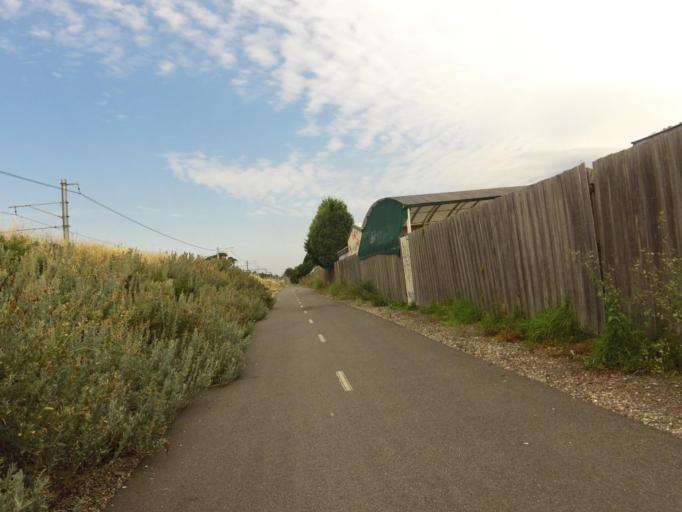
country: AU
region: Victoria
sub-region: Whittlesea
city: Epping
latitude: -37.6522
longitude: 145.0386
